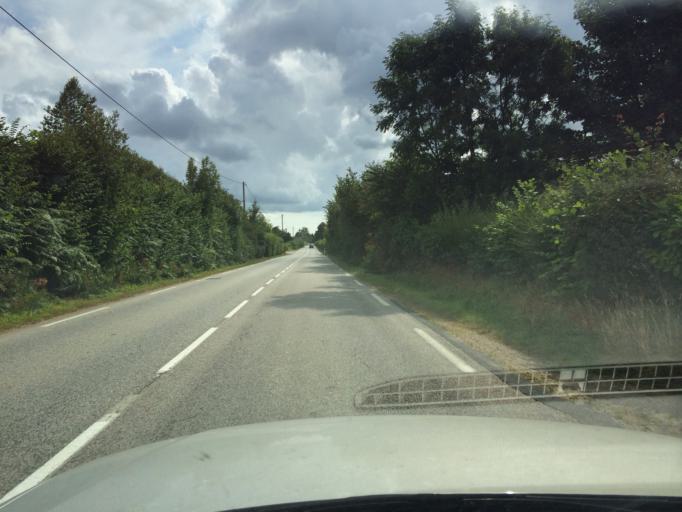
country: FR
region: Lower Normandy
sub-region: Departement de la Manche
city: Brix
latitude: 49.5638
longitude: -1.5841
